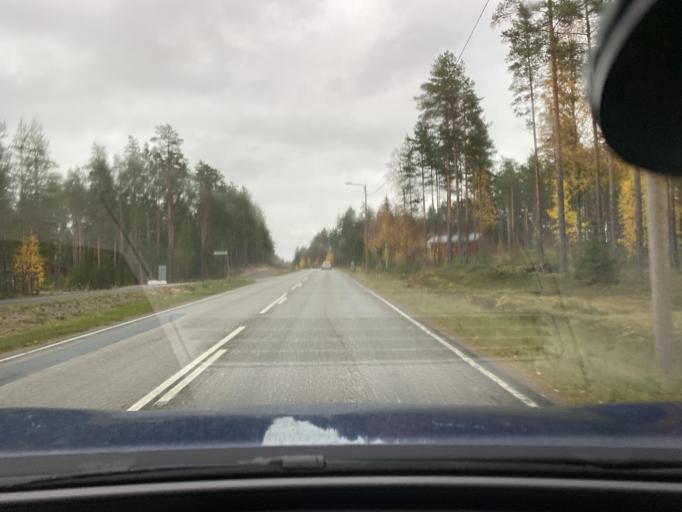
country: FI
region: Satakunta
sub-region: Rauma
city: Saekylae
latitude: 61.0593
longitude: 22.4760
